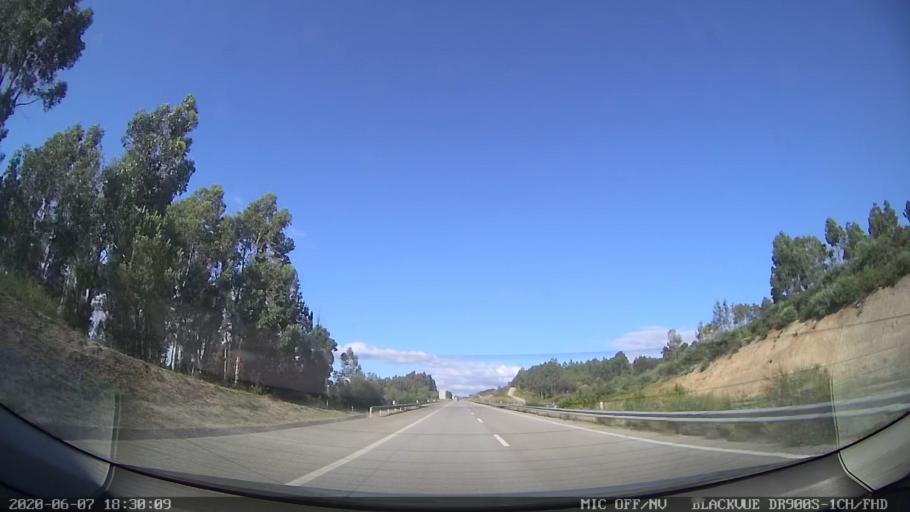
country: PT
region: Braga
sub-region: Fafe
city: Fafe
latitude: 41.4405
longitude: -8.1170
